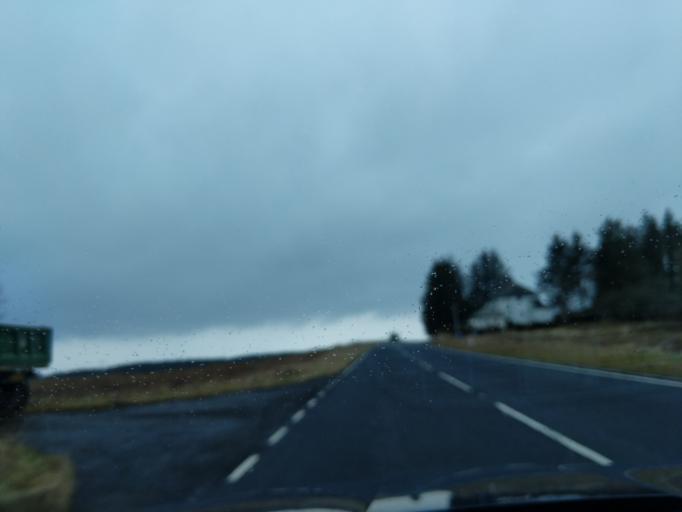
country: GB
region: England
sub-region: Northumberland
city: Corsenside
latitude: 55.1976
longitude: -2.0865
